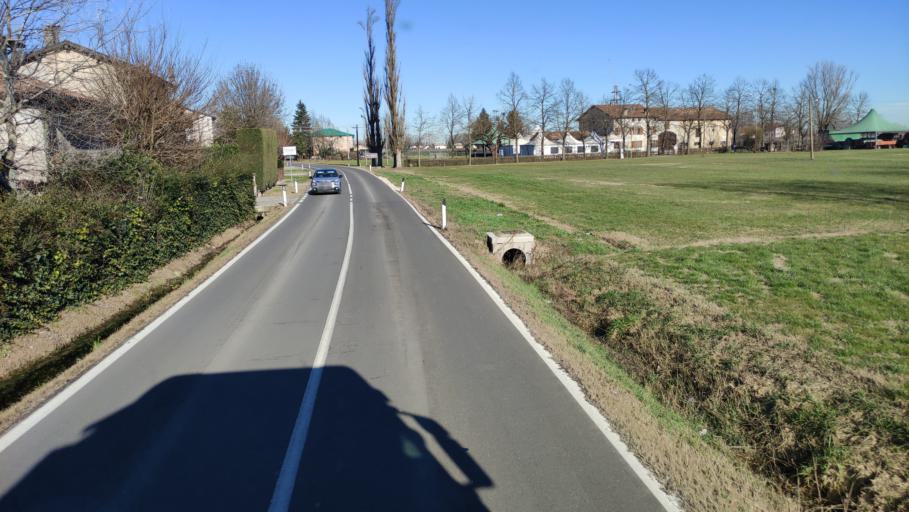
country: IT
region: Emilia-Romagna
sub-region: Provincia di Reggio Emilia
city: Rio Saliceto
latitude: 44.7990
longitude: 10.7789
